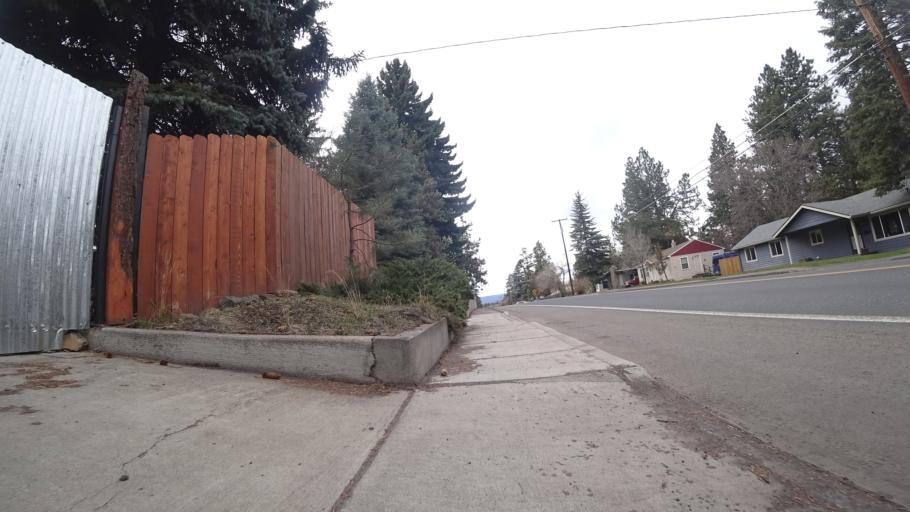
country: US
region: Oregon
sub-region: Deschutes County
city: Bend
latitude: 44.0559
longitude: -121.2960
